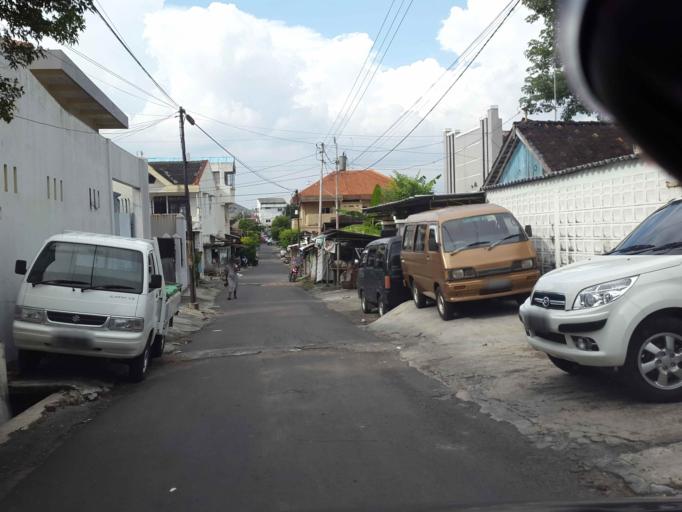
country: ID
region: Central Java
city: Surakarta
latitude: -7.5677
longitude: 110.8404
